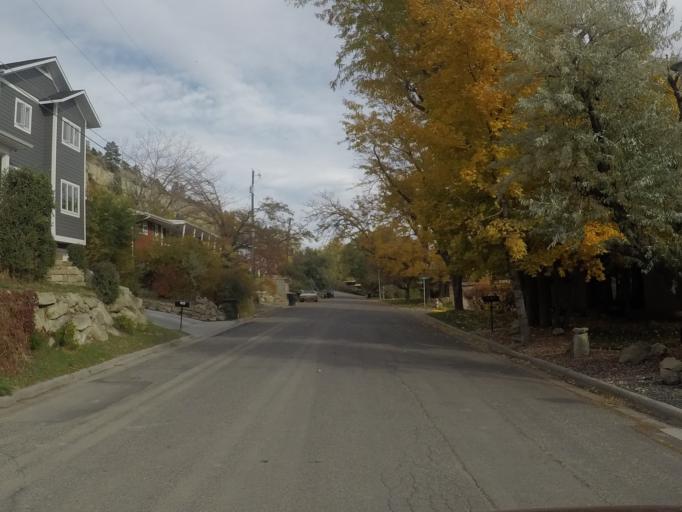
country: US
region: Montana
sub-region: Yellowstone County
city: Billings
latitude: 45.8011
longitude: -108.5518
